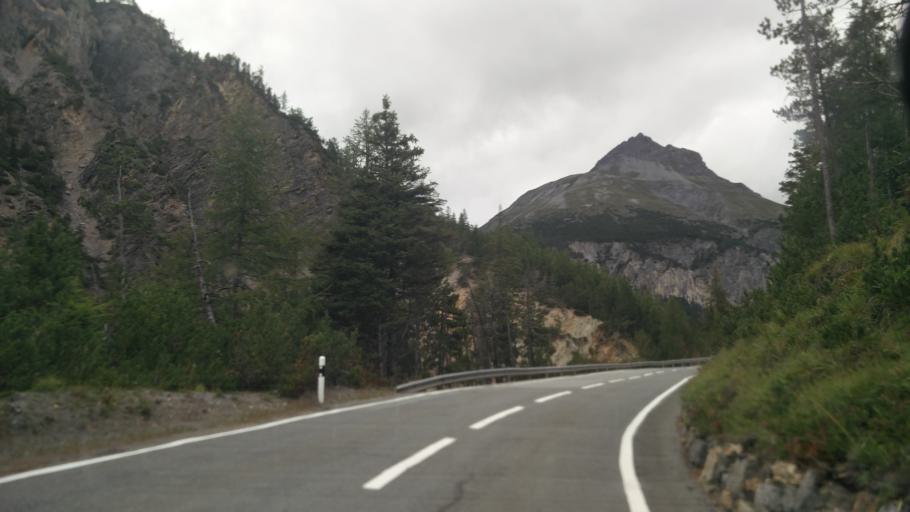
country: CH
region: Grisons
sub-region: Inn District
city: Zernez
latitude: 46.6553
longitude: 10.1906
